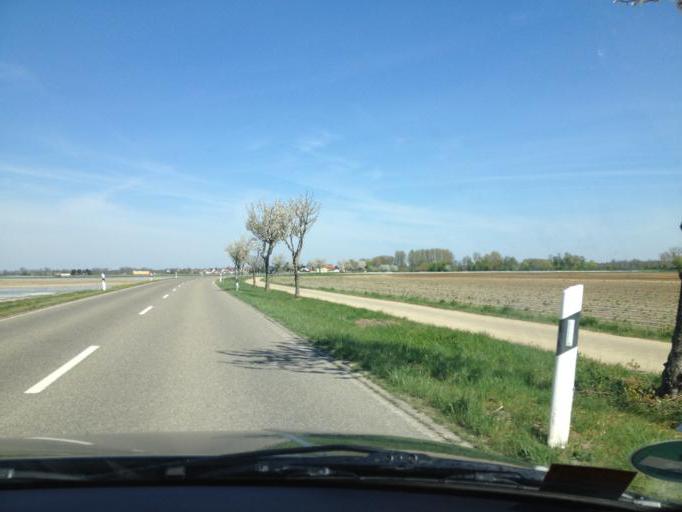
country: DE
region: Rheinland-Pfalz
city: Otterstadt
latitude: 49.3759
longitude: 8.4362
